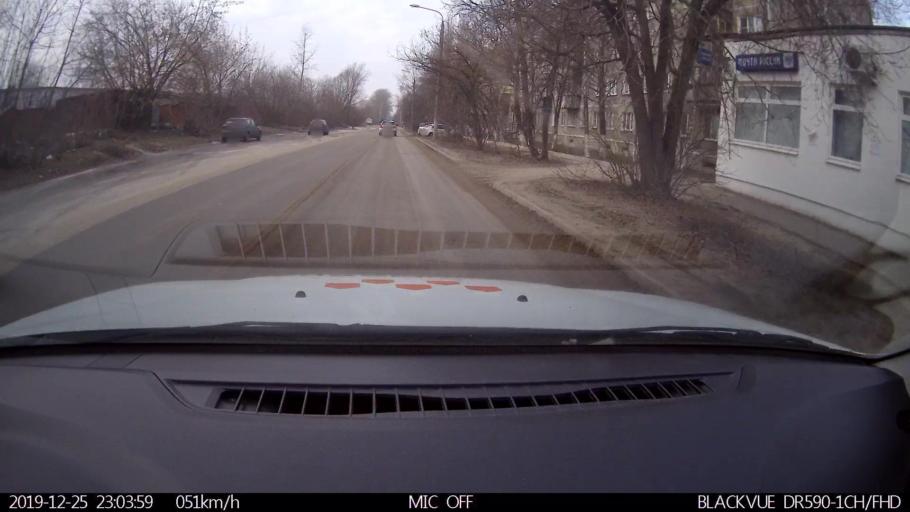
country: RU
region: Nizjnij Novgorod
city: Gorbatovka
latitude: 56.3563
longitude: 43.8163
